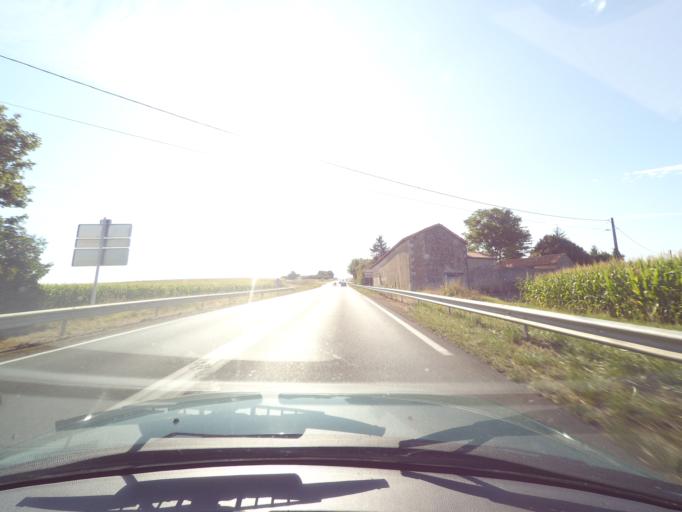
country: FR
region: Poitou-Charentes
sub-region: Departement de la Vienne
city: Cisse
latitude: 46.6411
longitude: 0.2012
